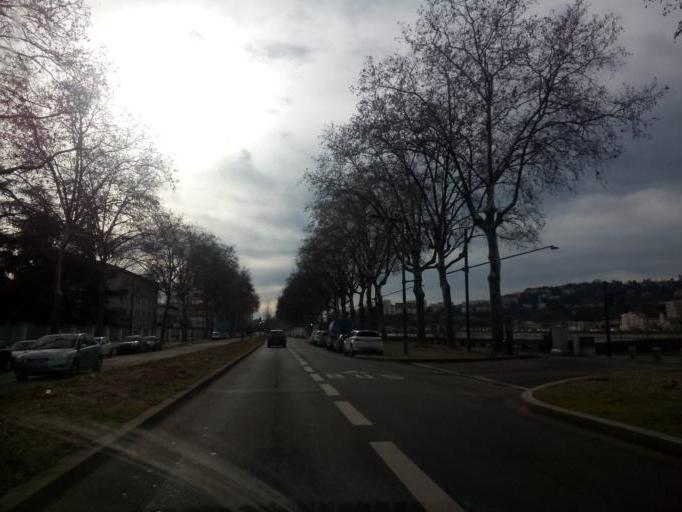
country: FR
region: Rhone-Alpes
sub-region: Departement du Rhone
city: Lyon
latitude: 45.7422
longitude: 4.8284
